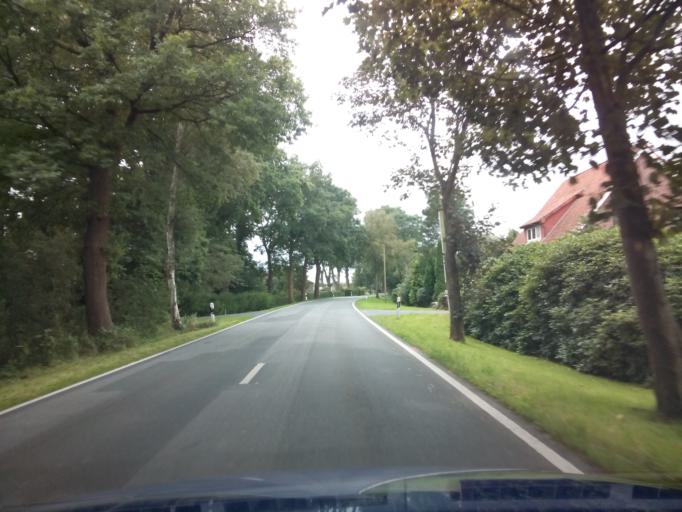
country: DE
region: Lower Saxony
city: Beverstedt
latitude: 53.4680
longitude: 8.8482
